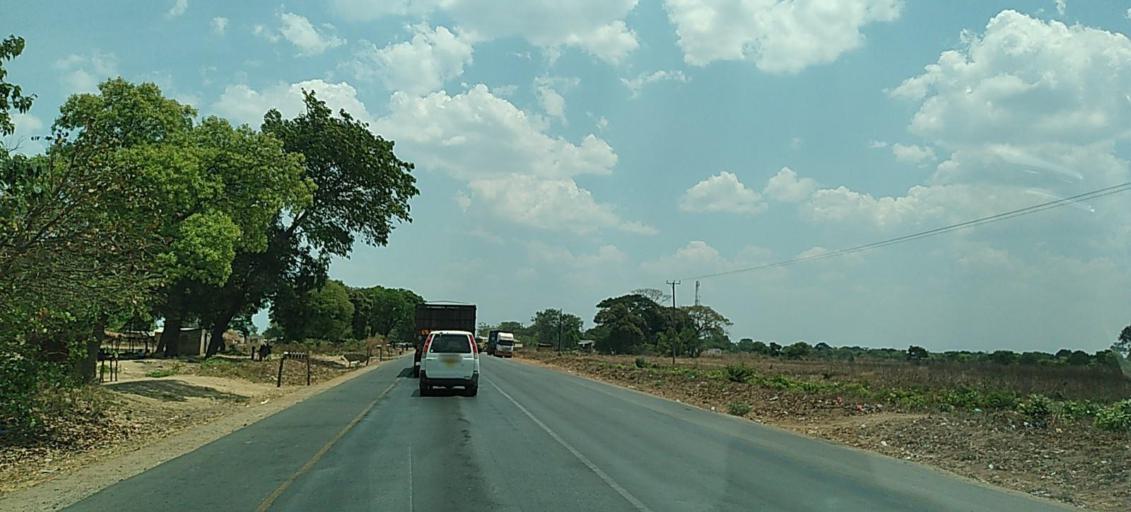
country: ZM
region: Central
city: Kabwe
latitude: -14.2194
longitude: 28.5774
